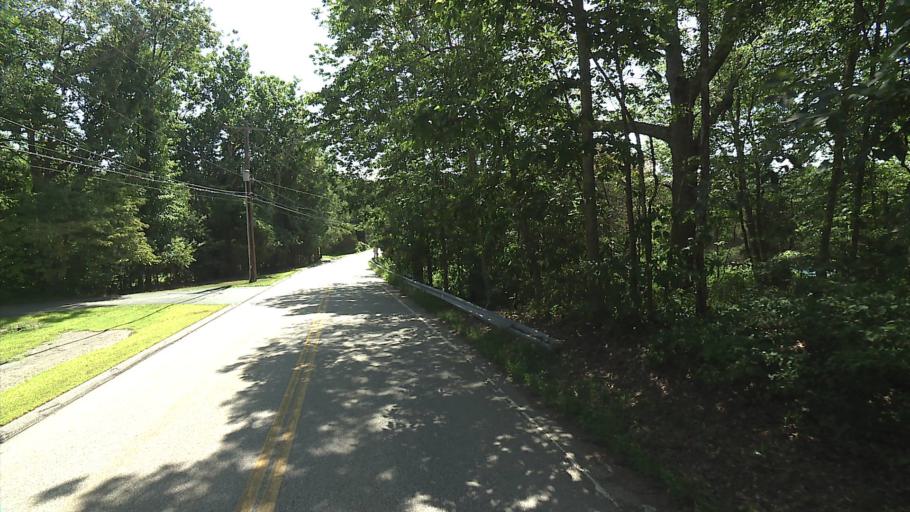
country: US
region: Connecticut
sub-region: New London County
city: Lisbon
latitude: 41.6075
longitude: -72.0214
